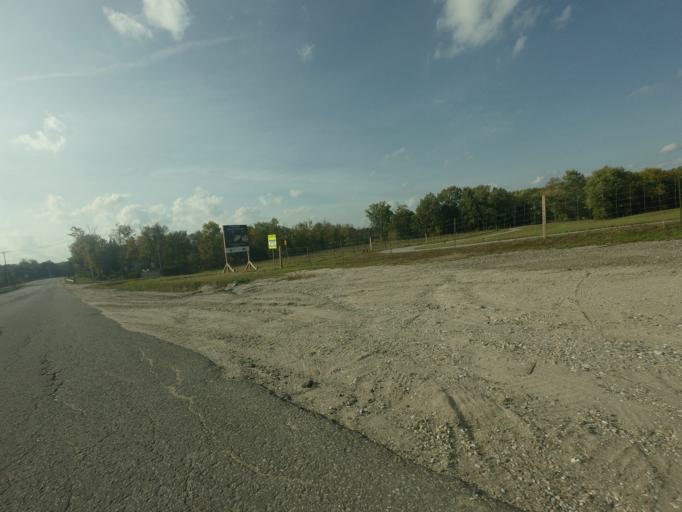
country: CA
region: Quebec
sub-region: Outaouais
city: Maniwaki
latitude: 46.3645
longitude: -75.9898
